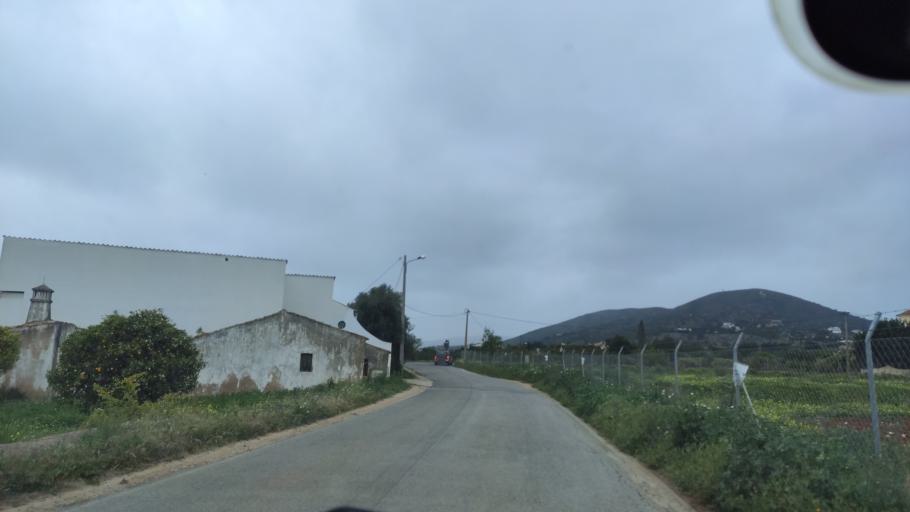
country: PT
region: Faro
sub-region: Faro
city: Santa Barbara de Nexe
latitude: 37.0859
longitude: -7.9157
